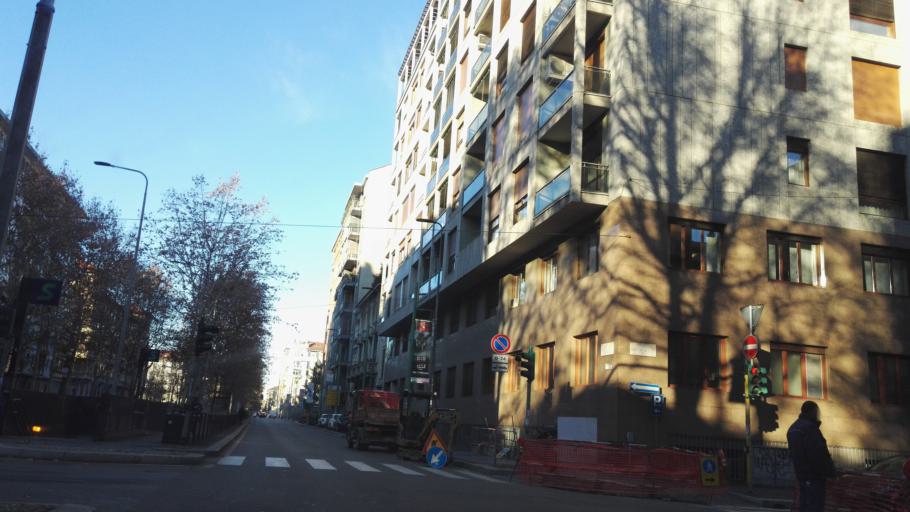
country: IT
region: Lombardy
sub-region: Citta metropolitana di Milano
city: Milano
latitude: 45.4654
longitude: 9.2174
